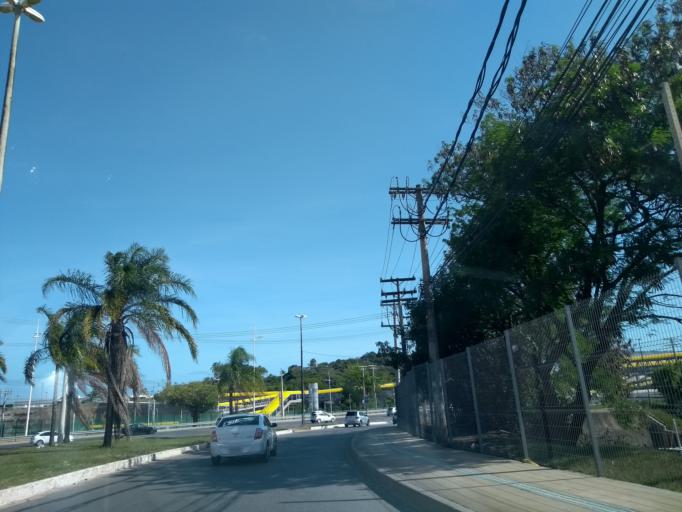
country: BR
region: Bahia
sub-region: Salvador
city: Salvador
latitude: -12.9428
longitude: -38.4206
